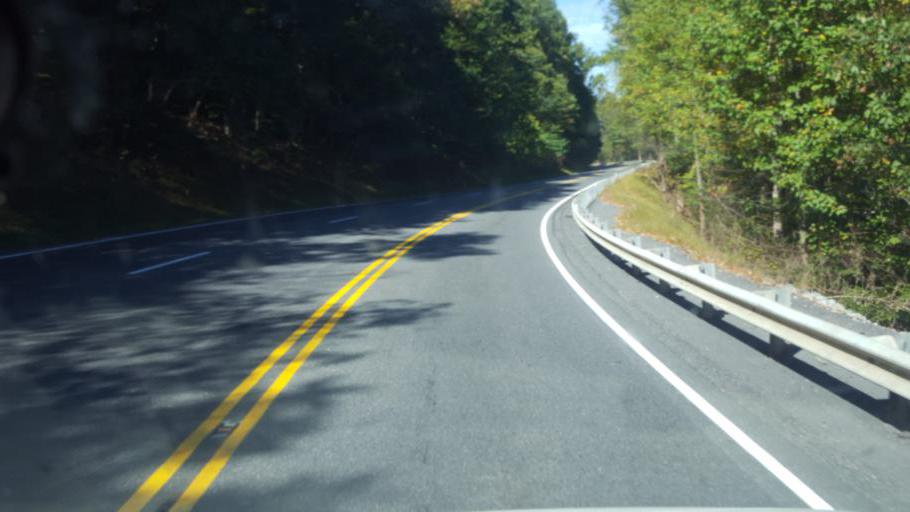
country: US
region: Virginia
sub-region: Rockingham County
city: Elkton
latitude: 38.3633
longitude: -78.5544
